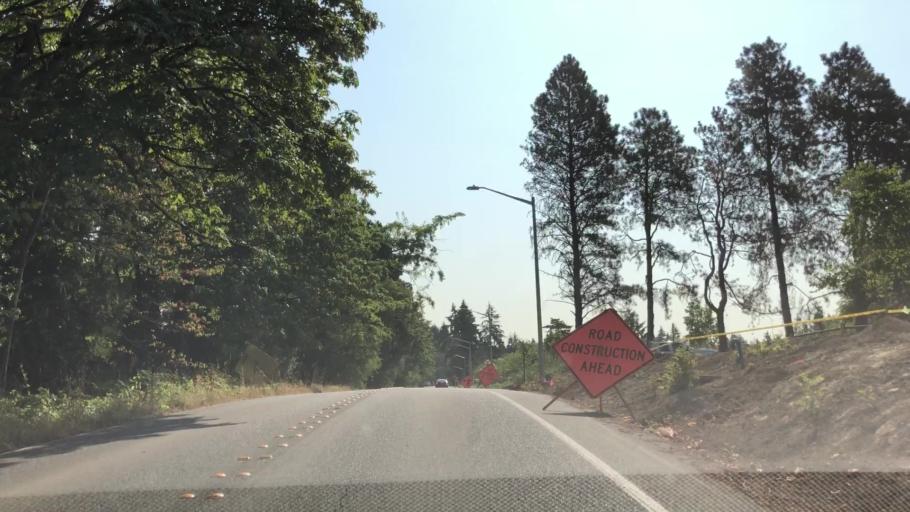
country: US
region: Washington
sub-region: King County
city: Bellevue
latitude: 47.6100
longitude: -122.1809
